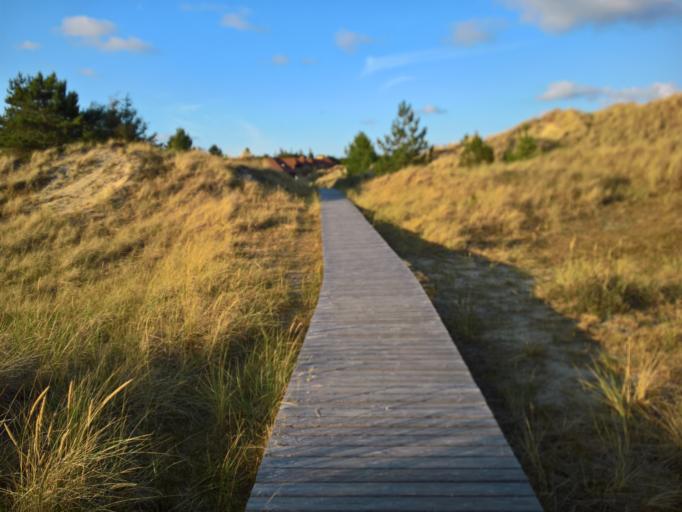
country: DE
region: Schleswig-Holstein
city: Wittdun
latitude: 54.6263
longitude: 8.3749
